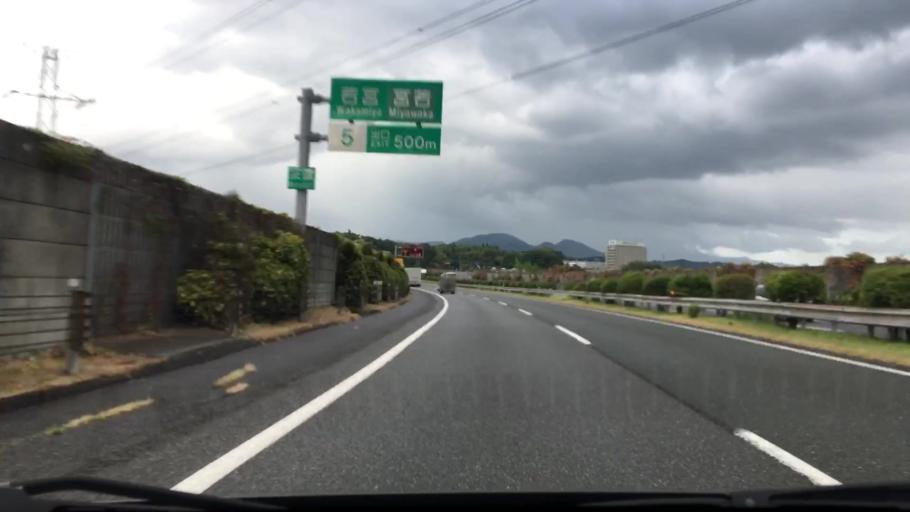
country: JP
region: Fukuoka
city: Miyata
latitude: 33.7460
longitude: 130.6010
